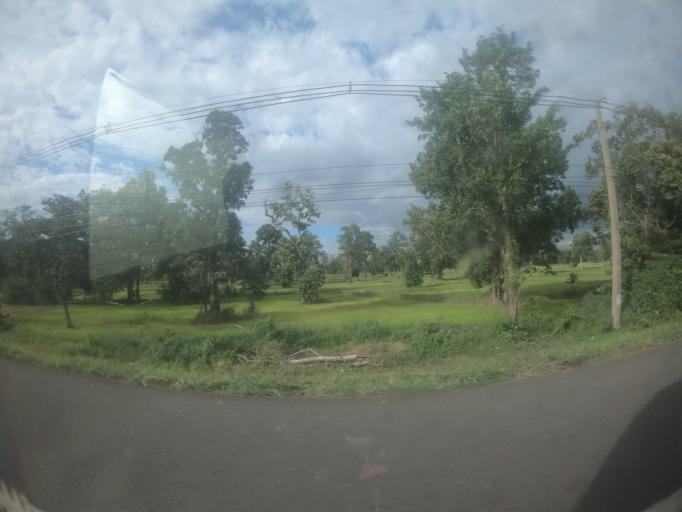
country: TH
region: Surin
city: Prasat
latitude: 14.5855
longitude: 103.4720
